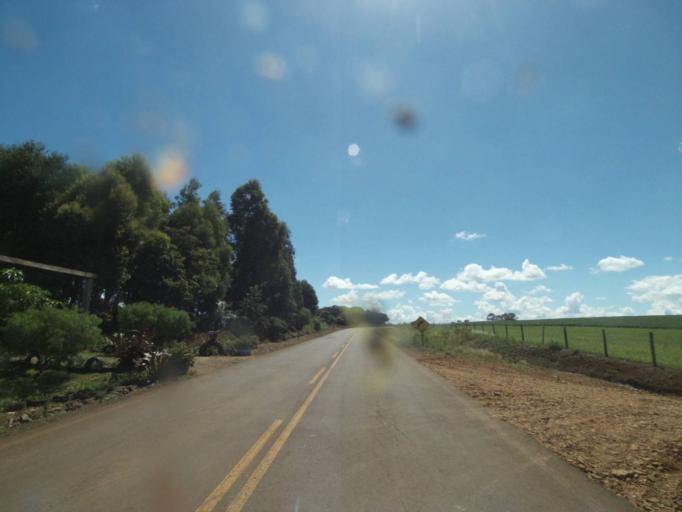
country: BR
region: Parana
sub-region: Pinhao
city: Pinhao
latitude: -25.8132
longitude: -52.0642
